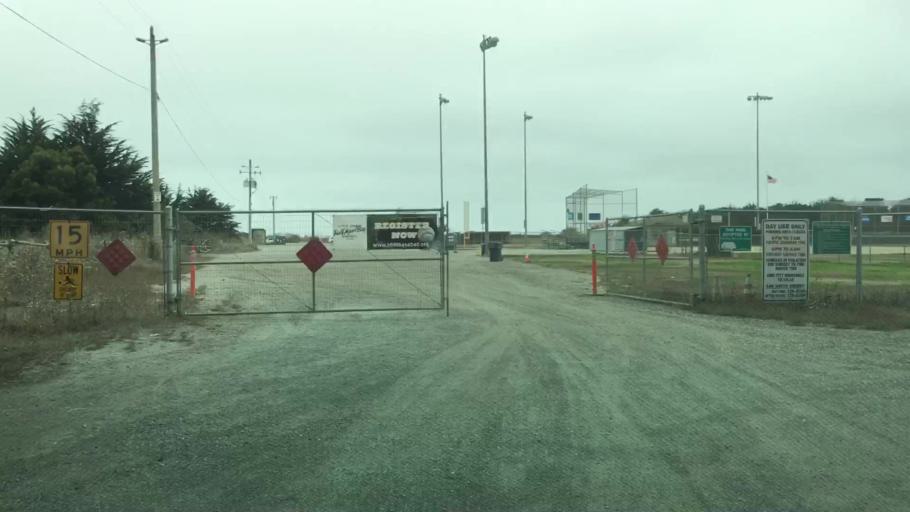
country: US
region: California
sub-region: San Mateo County
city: Half Moon Bay
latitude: 37.4469
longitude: -122.4353
